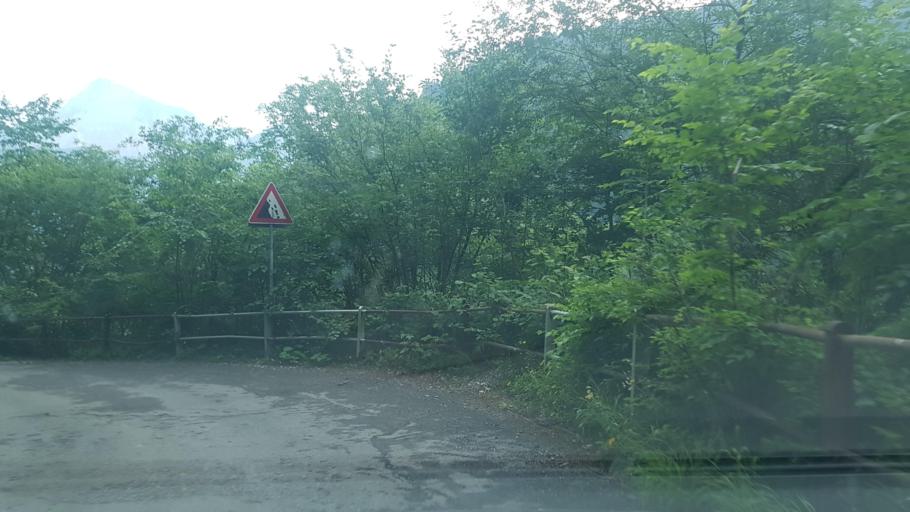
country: IT
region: Friuli Venezia Giulia
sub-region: Provincia di Udine
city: Paularo
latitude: 46.5524
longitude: 13.1225
